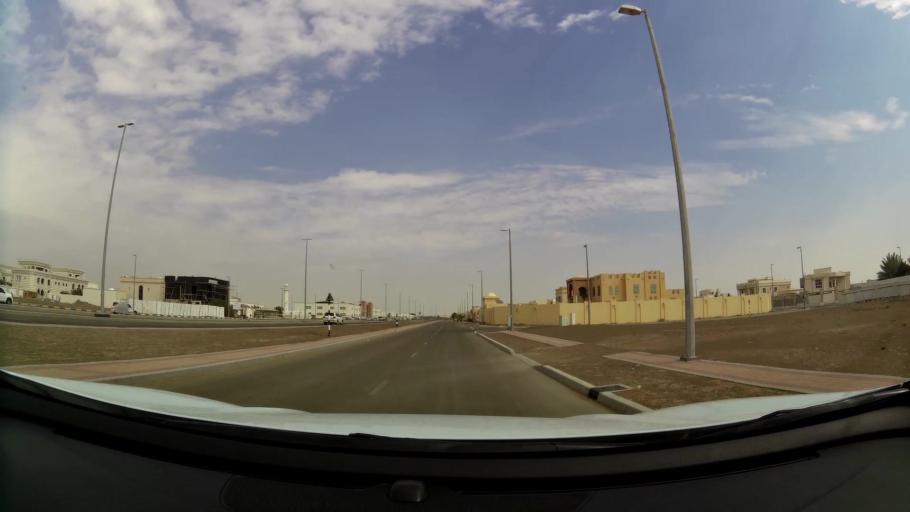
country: AE
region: Abu Dhabi
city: Al Ain
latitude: 24.1986
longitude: 55.8046
